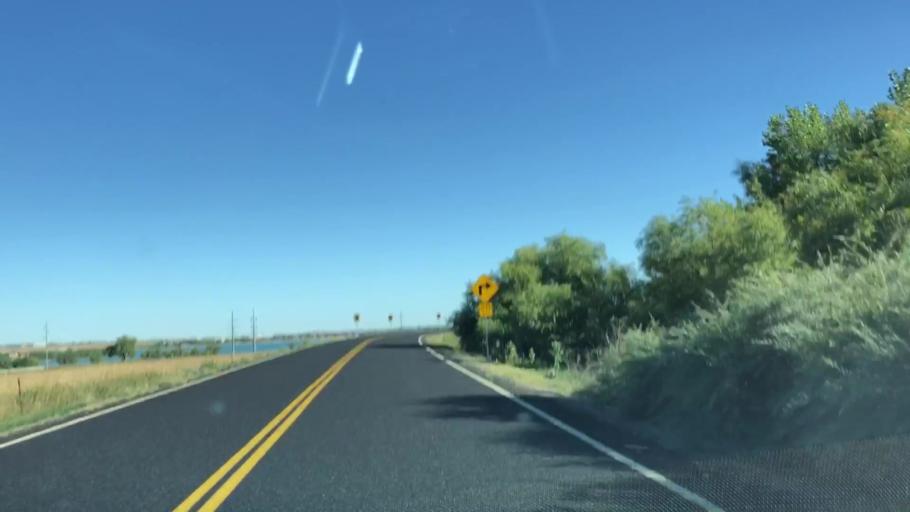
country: US
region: Colorado
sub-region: Larimer County
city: Loveland
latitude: 40.4625
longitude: -105.0501
